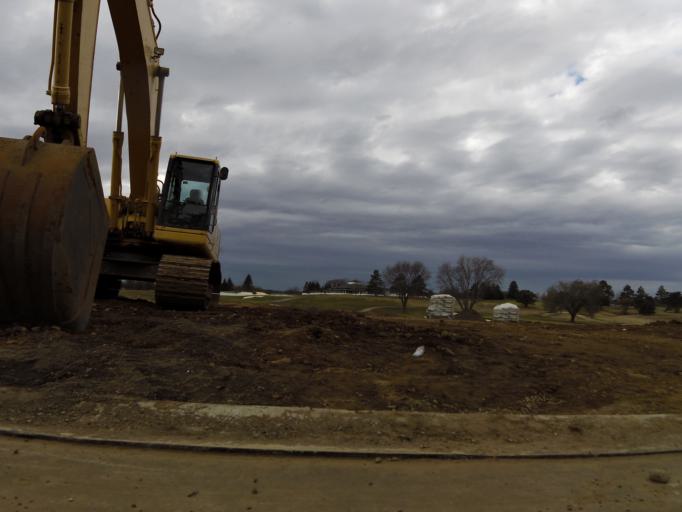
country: US
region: Minnesota
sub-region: Washington County
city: Lake Elmo
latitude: 44.9740
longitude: -92.8652
